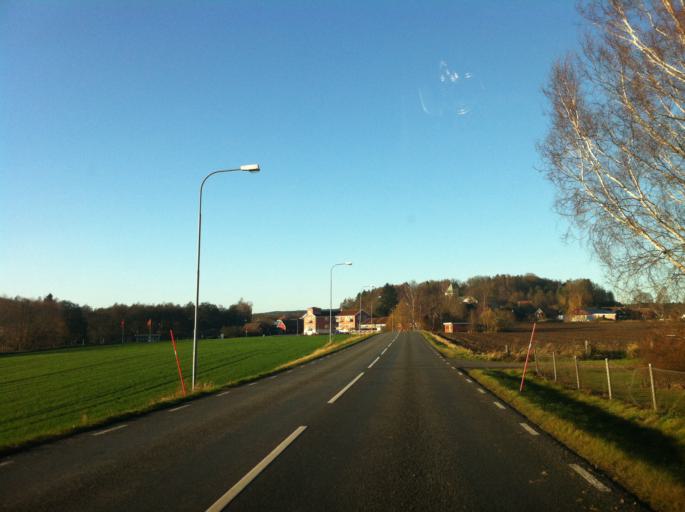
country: SE
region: Skane
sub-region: Bromolla Kommun
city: Nasum
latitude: 56.1602
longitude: 14.4467
